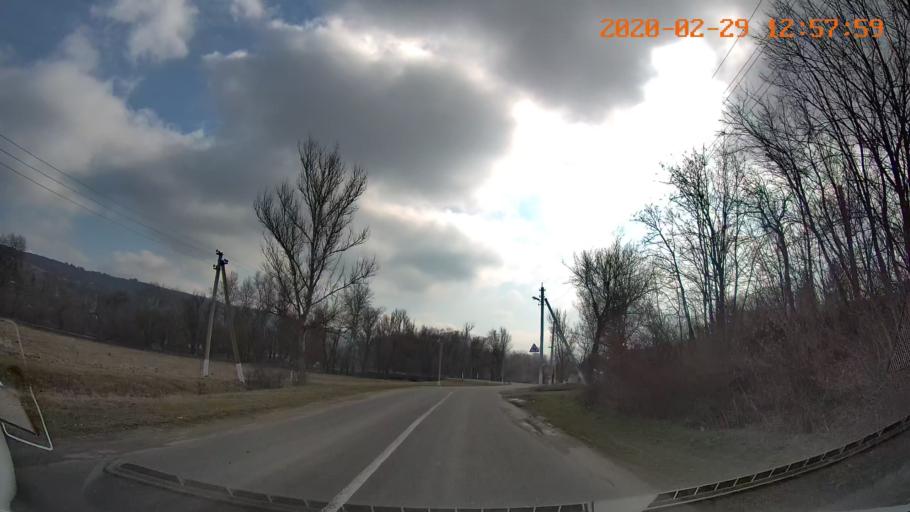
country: MD
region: Telenesti
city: Camenca
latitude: 48.0725
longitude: 28.7176
